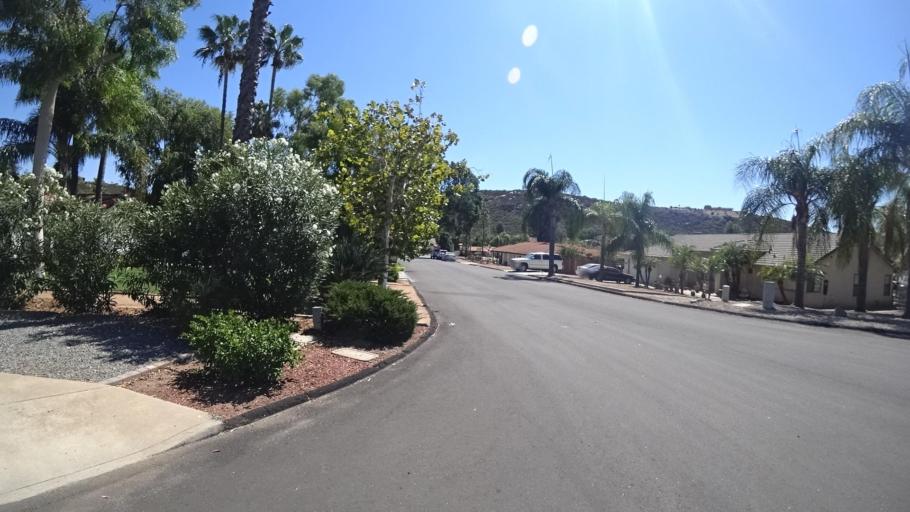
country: US
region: California
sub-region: San Diego County
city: San Diego Country Estates
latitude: 33.0122
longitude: -116.8108
